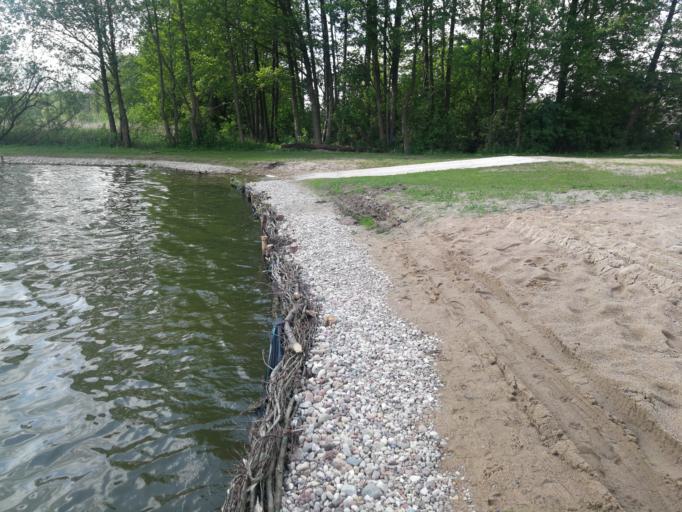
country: PL
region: Warmian-Masurian Voivodeship
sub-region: Powiat dzialdowski
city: Rybno
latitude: 53.3786
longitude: 19.9490
